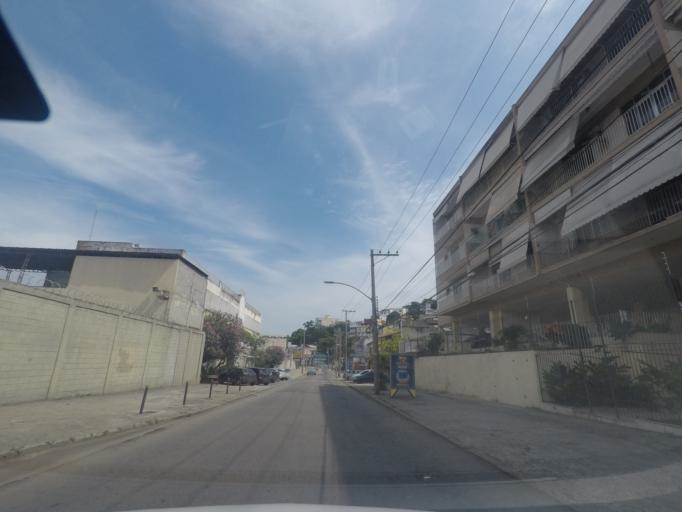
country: BR
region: Rio de Janeiro
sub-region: Rio De Janeiro
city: Rio de Janeiro
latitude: -22.8145
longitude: -43.1892
